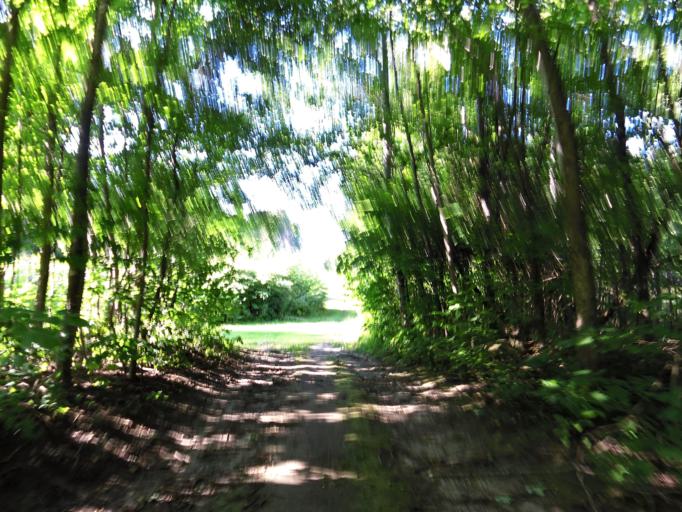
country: CA
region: Ontario
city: Ottawa
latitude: 45.4263
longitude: -75.7415
